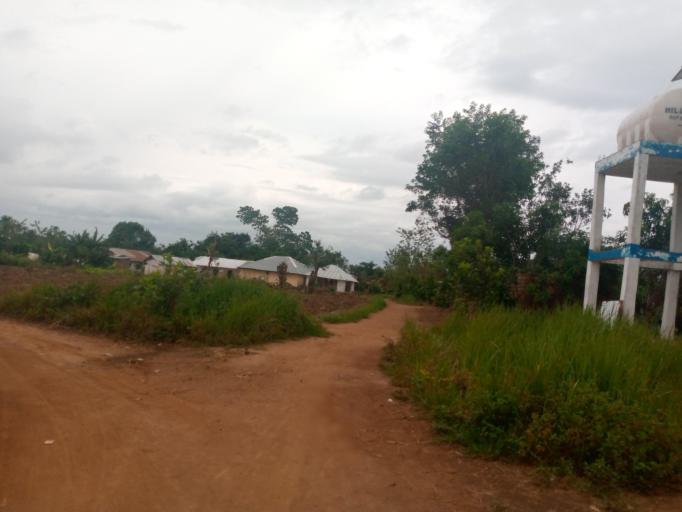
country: SL
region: Southern Province
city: Sumbuya
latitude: 7.6008
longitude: -12.1630
